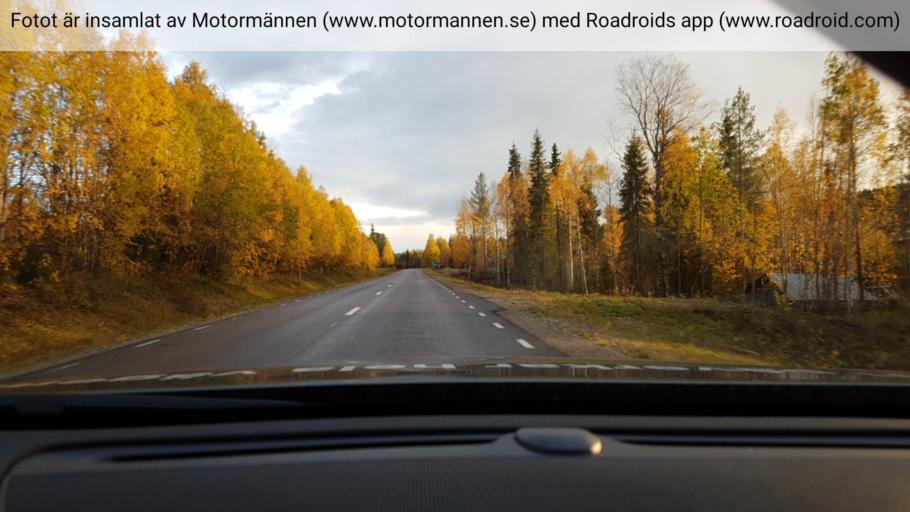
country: SE
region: Norrbotten
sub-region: Overkalix Kommun
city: OEverkalix
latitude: 66.5972
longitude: 22.7605
